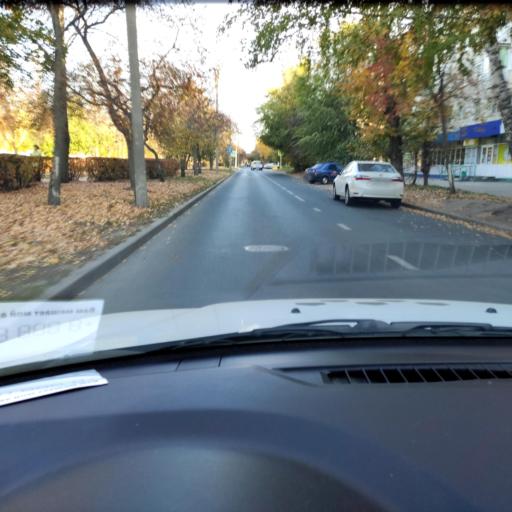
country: RU
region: Samara
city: Tol'yatti
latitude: 53.5019
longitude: 49.4142
